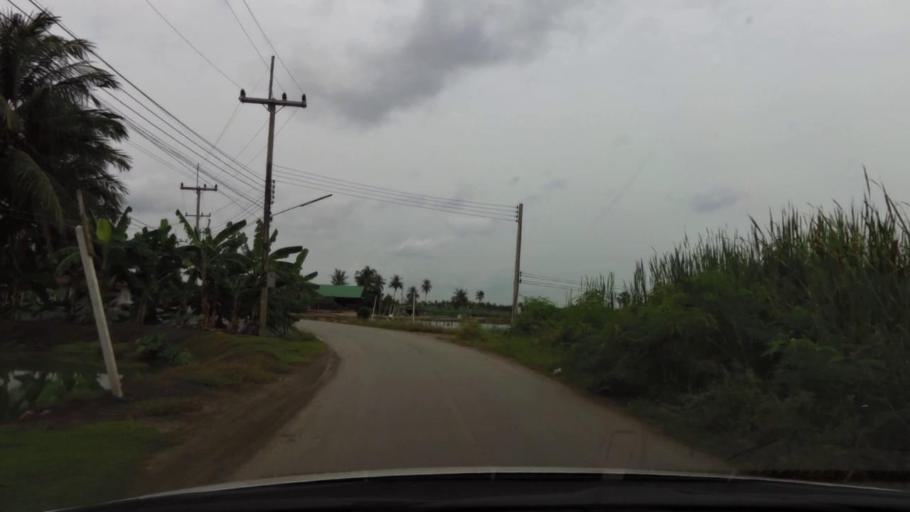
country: TH
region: Samut Sakhon
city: Ban Phaeo
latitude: 13.6263
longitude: 100.0259
